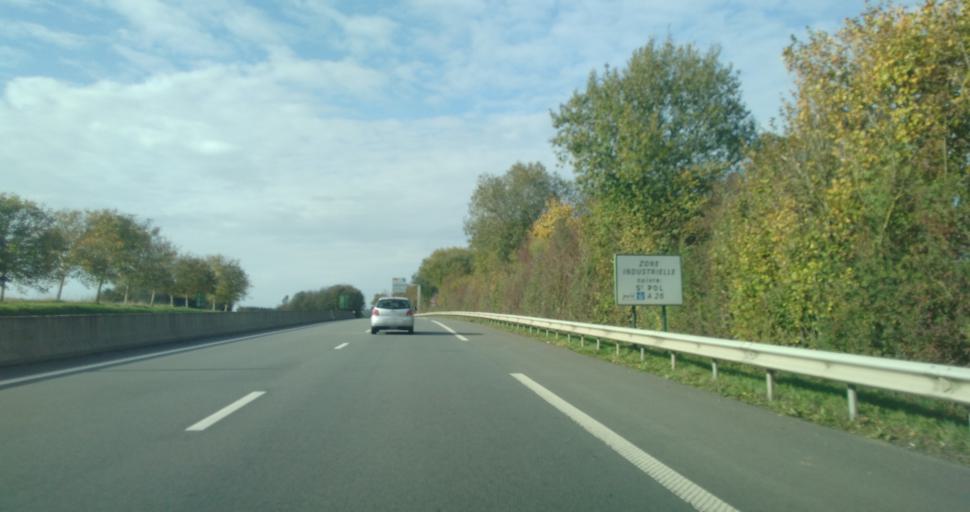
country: FR
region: Nord-Pas-de-Calais
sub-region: Departement du Pas-de-Calais
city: Saint-Pol-sur-Ternoise
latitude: 50.3651
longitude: 2.4098
